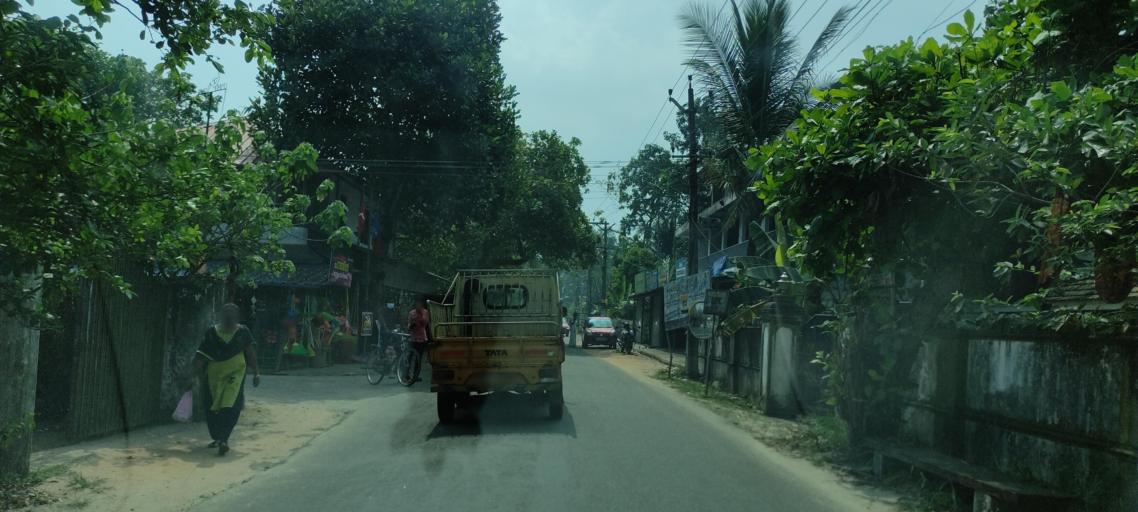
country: IN
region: Kerala
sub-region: Alappuzha
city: Shertallai
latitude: 9.6154
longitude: 76.3474
